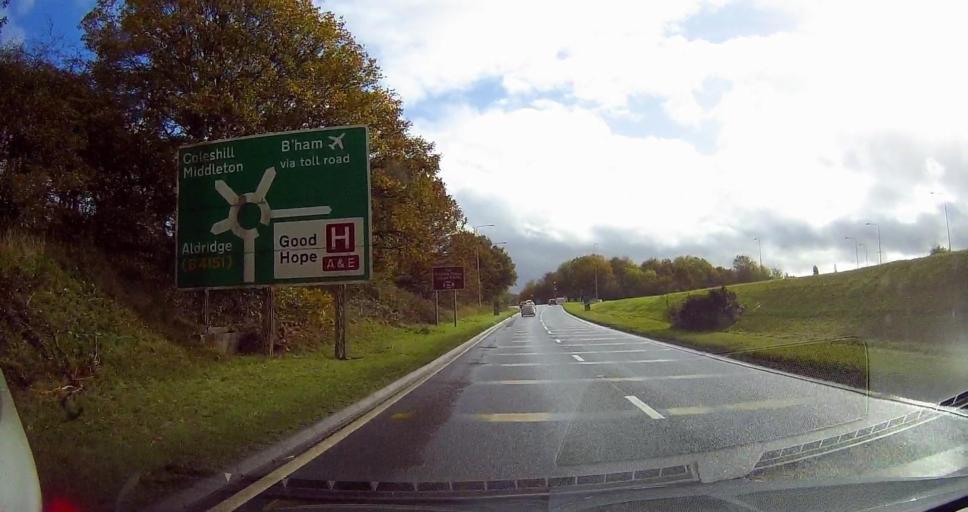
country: GB
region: England
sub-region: City and Borough of Birmingham
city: Sutton Coldfield
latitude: 52.5925
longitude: -1.7852
